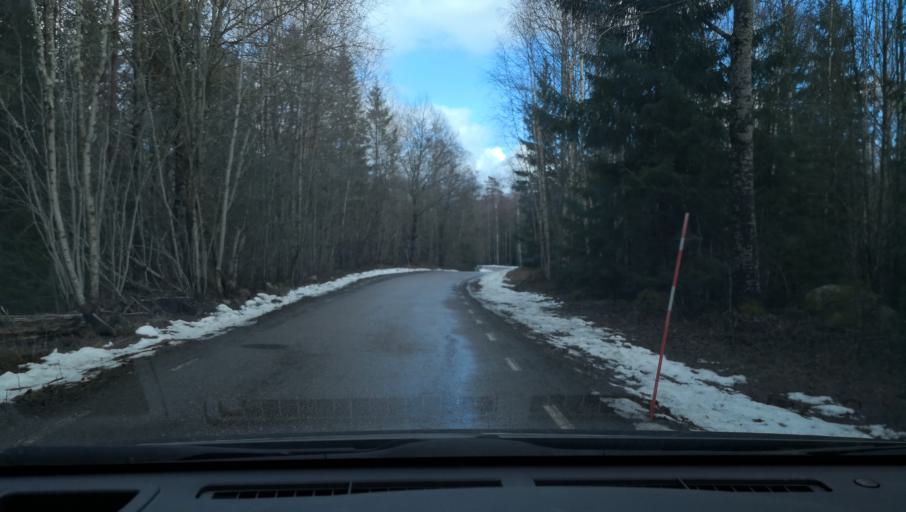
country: SE
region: Vaestmanland
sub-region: Arboga Kommun
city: Arboga
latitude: 59.3364
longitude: 15.7106
